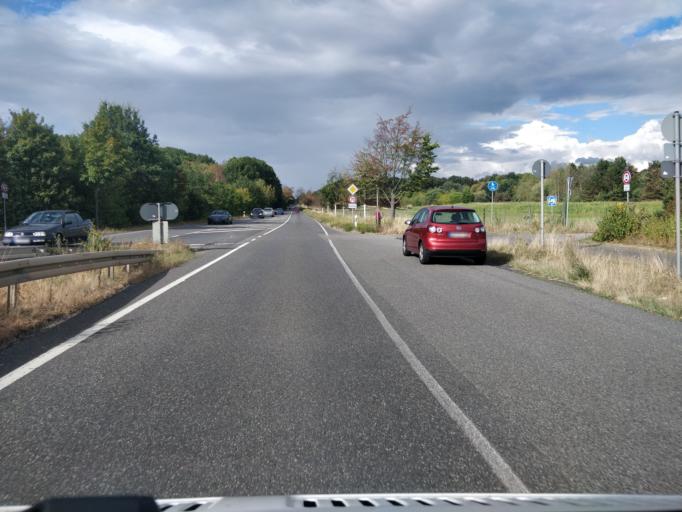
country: DE
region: North Rhine-Westphalia
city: Meckenheim
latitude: 50.6424
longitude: 7.0383
